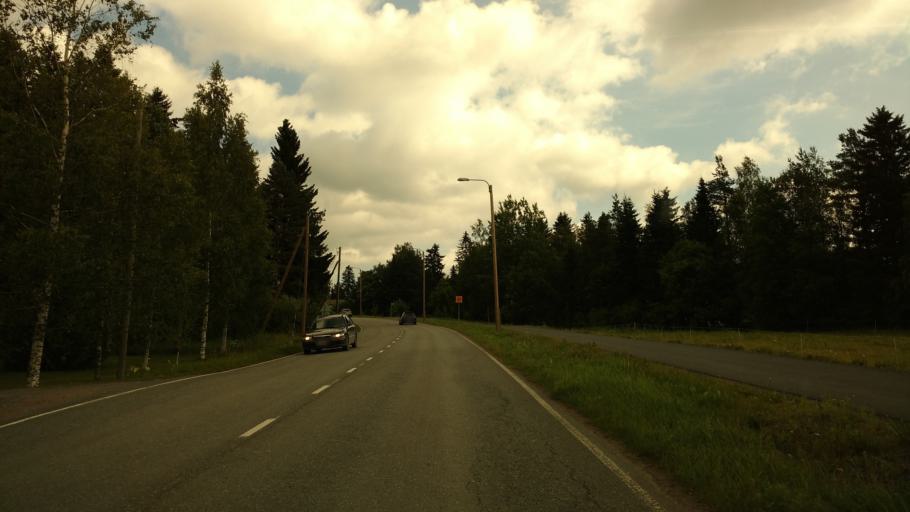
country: FI
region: Haeme
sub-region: Forssa
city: Ypaejae
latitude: 60.7972
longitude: 23.2779
